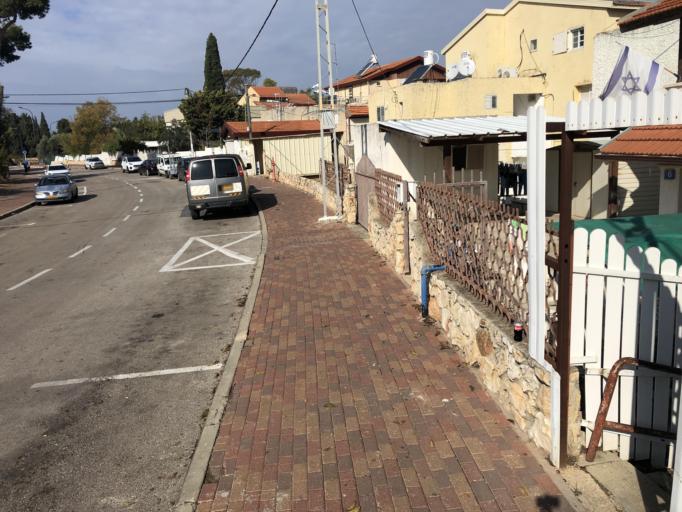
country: IL
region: Northern District
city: `Akko
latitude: 32.9394
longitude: 35.0940
